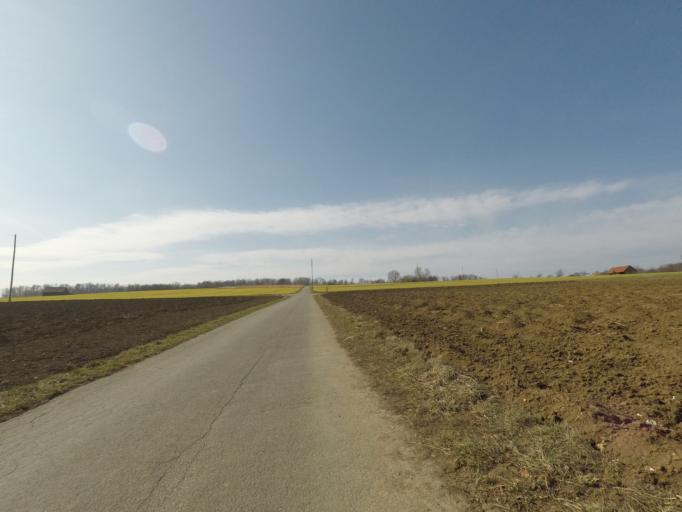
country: DE
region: Baden-Wuerttemberg
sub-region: Tuebingen Region
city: Metzingen
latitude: 48.5335
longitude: 9.2600
